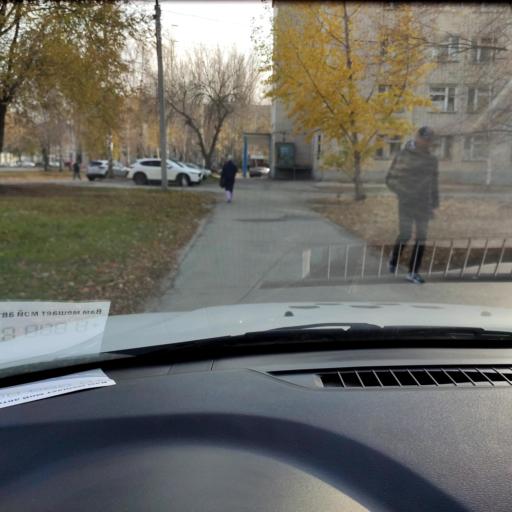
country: RU
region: Samara
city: Tol'yatti
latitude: 53.5024
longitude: 49.4119
